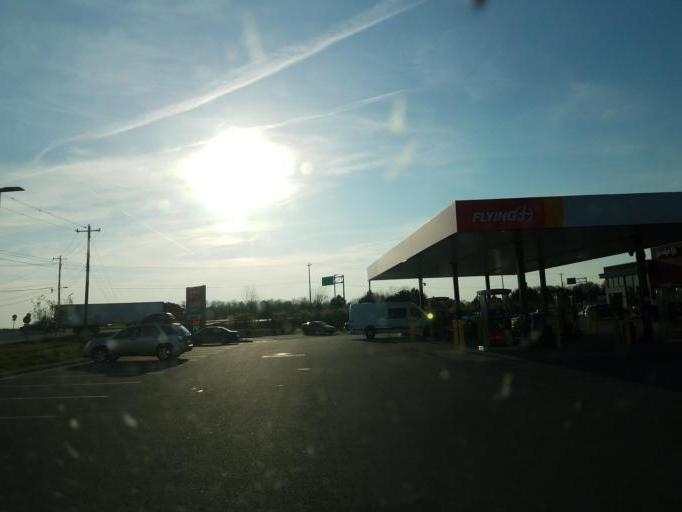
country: US
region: Ohio
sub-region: Warren County
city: Lebanon
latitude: 39.4110
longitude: -84.1500
